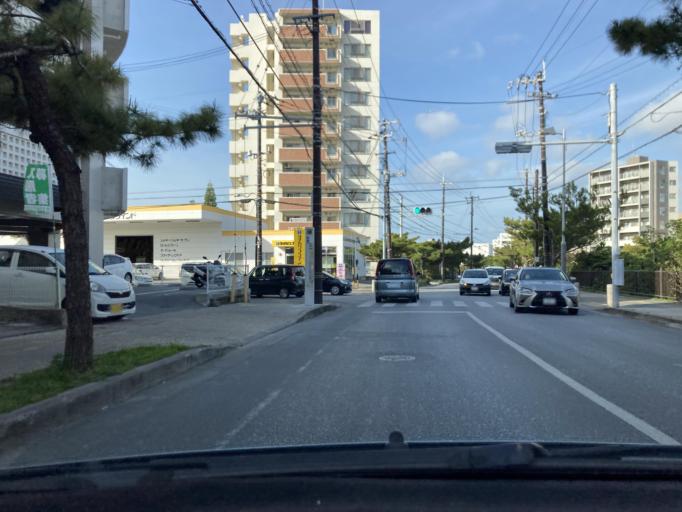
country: JP
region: Okinawa
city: Naha-shi
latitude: 26.2344
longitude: 127.6954
